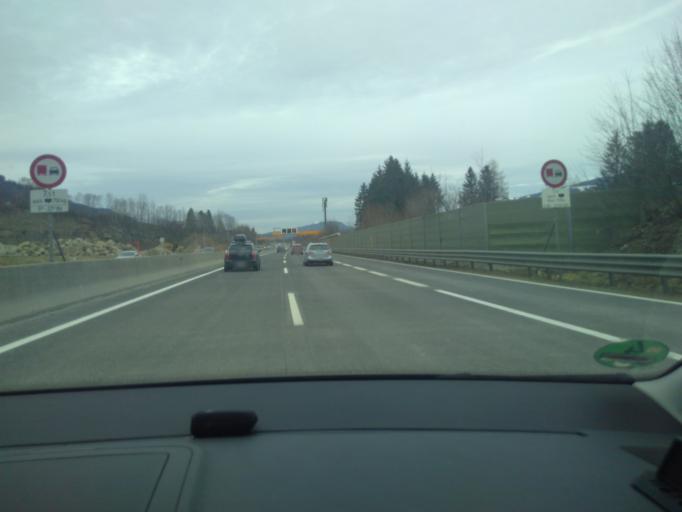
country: AT
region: Salzburg
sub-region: Politischer Bezirk Hallein
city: Golling an der Salzach
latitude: 47.5939
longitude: 13.1521
